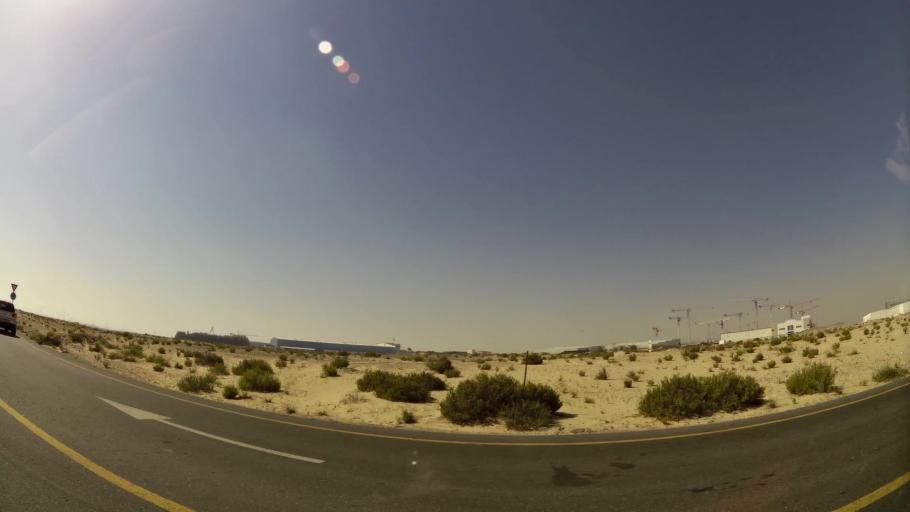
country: AE
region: Dubai
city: Dubai
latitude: 24.9254
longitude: 55.0576
